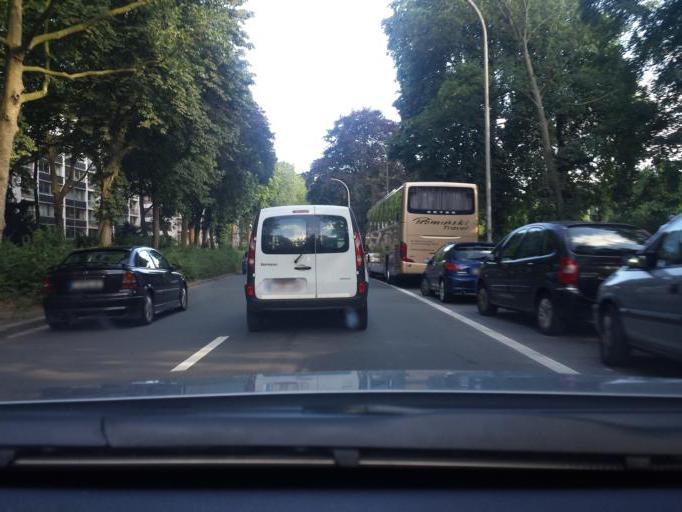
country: BE
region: Flanders
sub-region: Provincie Antwerpen
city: Antwerpen
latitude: 51.2130
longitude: 4.4162
